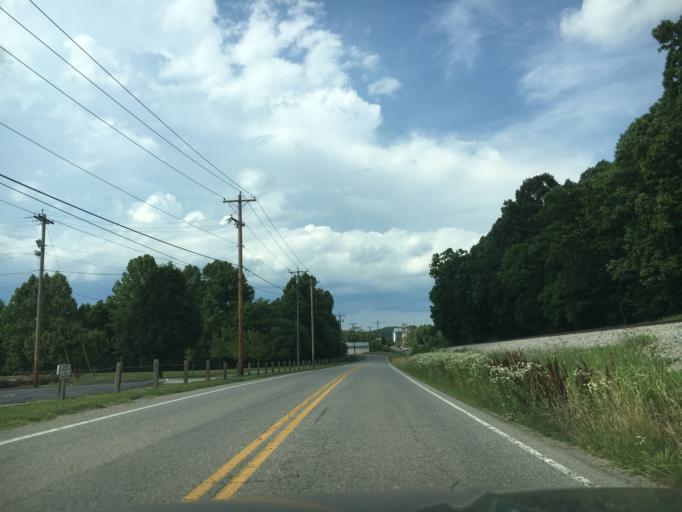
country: US
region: Virginia
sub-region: Roanoke County
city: Cave Spring
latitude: 37.1981
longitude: -79.9992
